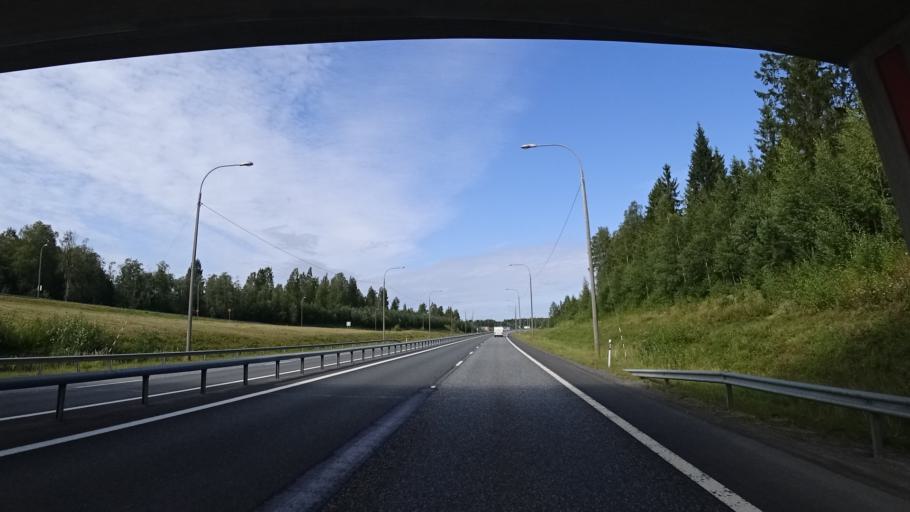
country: FI
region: North Karelia
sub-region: Joensuu
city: Joensuu
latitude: 62.5438
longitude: 29.8465
